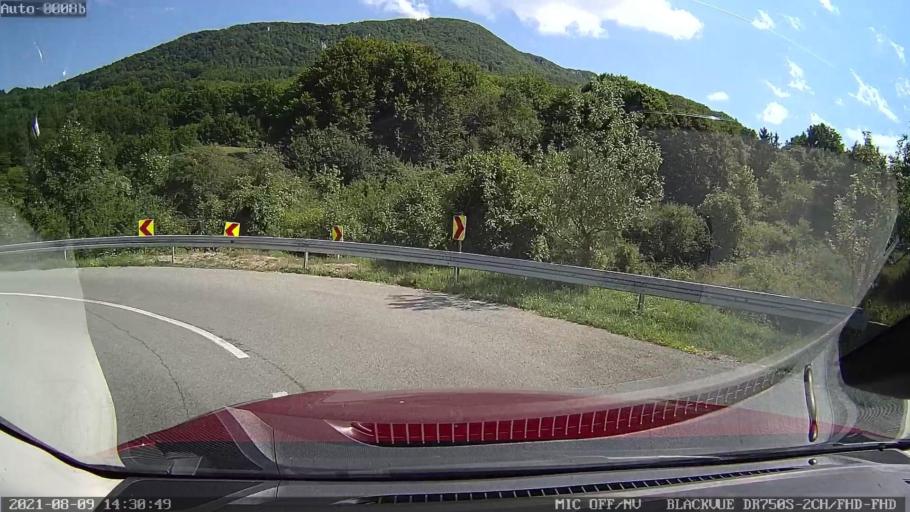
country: HR
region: Istarska
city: Lovran
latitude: 45.3060
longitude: 14.1954
